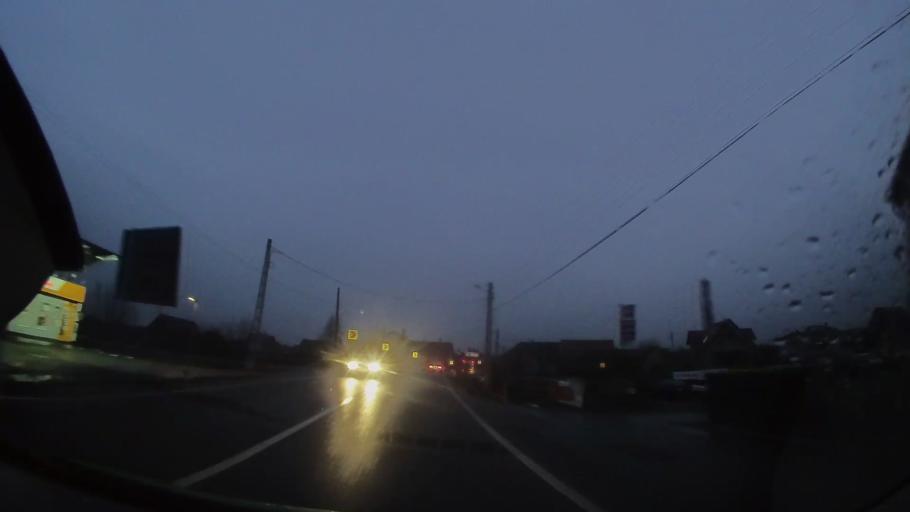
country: RO
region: Harghita
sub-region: Comuna Ditrau
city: Ditrau
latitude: 46.8070
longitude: 25.4931
